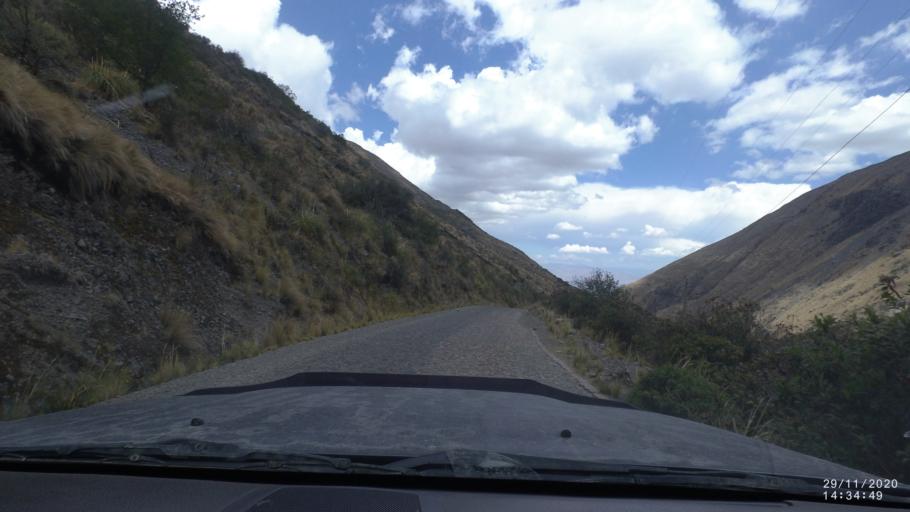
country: BO
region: Cochabamba
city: Sipe Sipe
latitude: -17.2683
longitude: -66.3411
